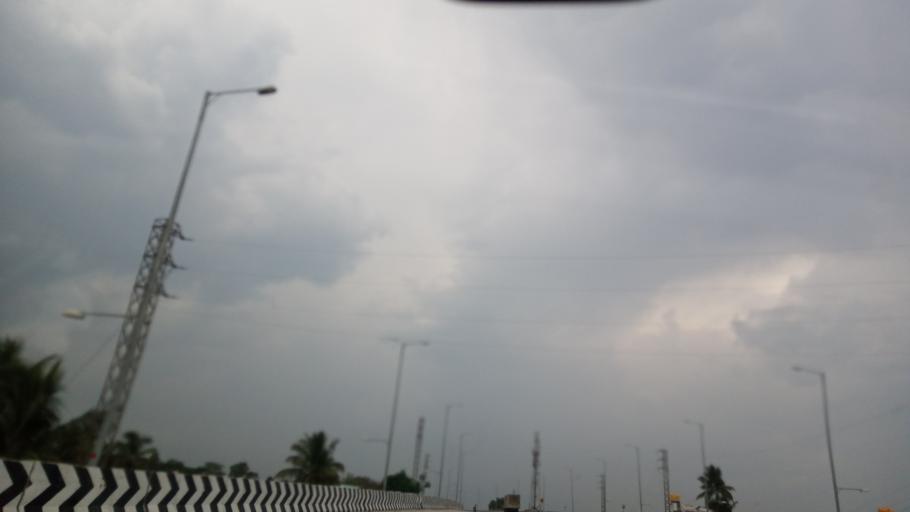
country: IN
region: Andhra Pradesh
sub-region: Chittoor
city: Palmaner
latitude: 13.1931
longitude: 78.5821
